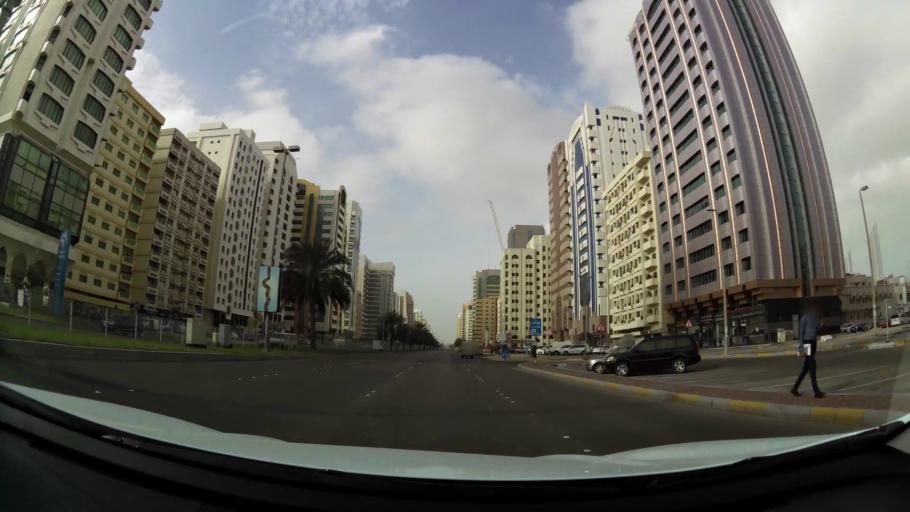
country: AE
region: Abu Dhabi
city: Abu Dhabi
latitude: 24.4825
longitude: 54.3747
